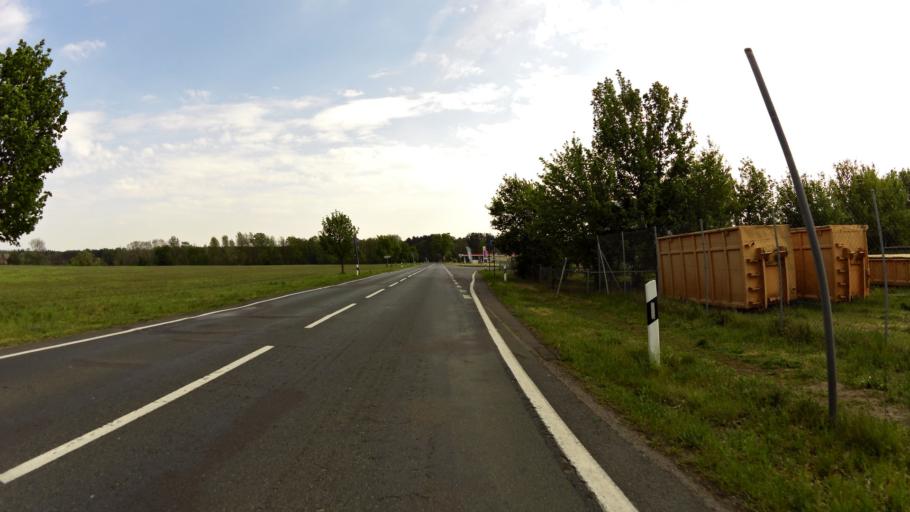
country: DE
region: Brandenburg
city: Spreenhagen
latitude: 52.3271
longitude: 13.8991
